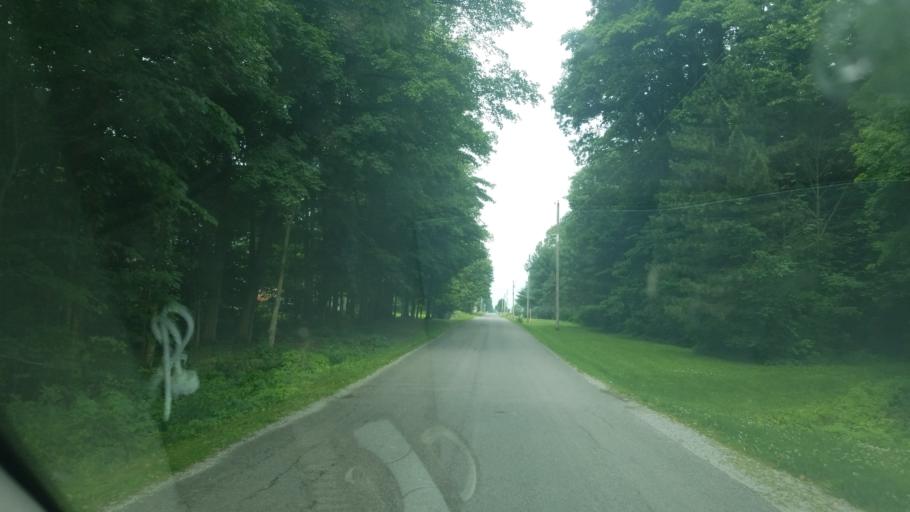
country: US
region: Ohio
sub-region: Seneca County
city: Fostoria
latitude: 41.0501
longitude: -83.4590
